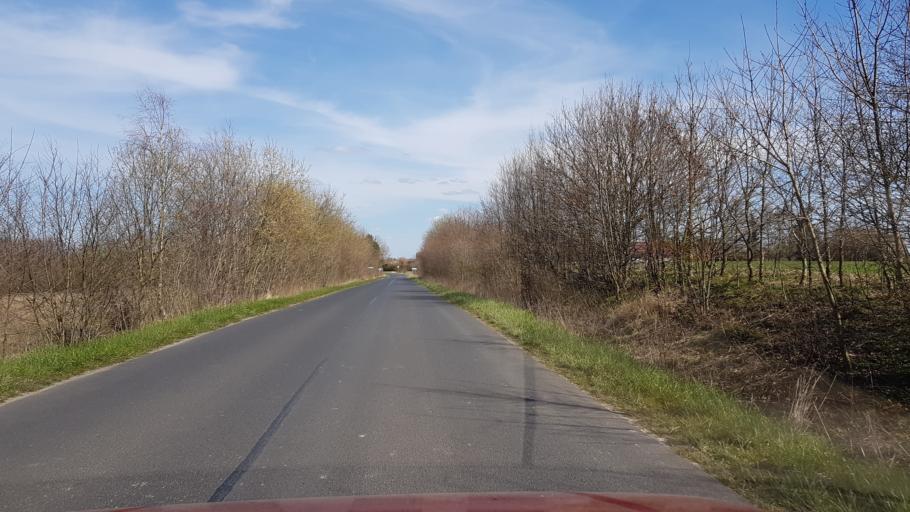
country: PL
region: West Pomeranian Voivodeship
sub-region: Powiat koszalinski
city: Mielno
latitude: 54.1721
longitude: 16.0014
